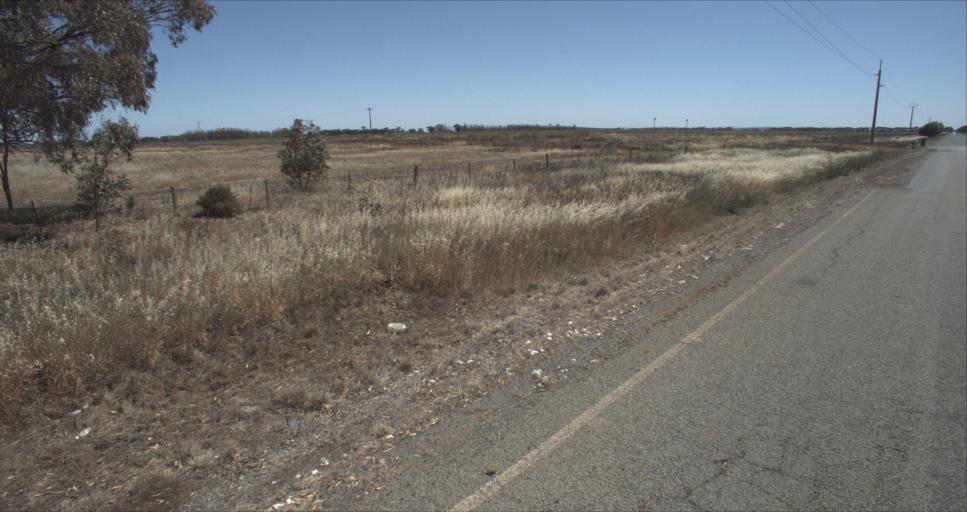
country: AU
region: New South Wales
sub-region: Leeton
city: Leeton
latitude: -34.4939
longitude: 146.2882
